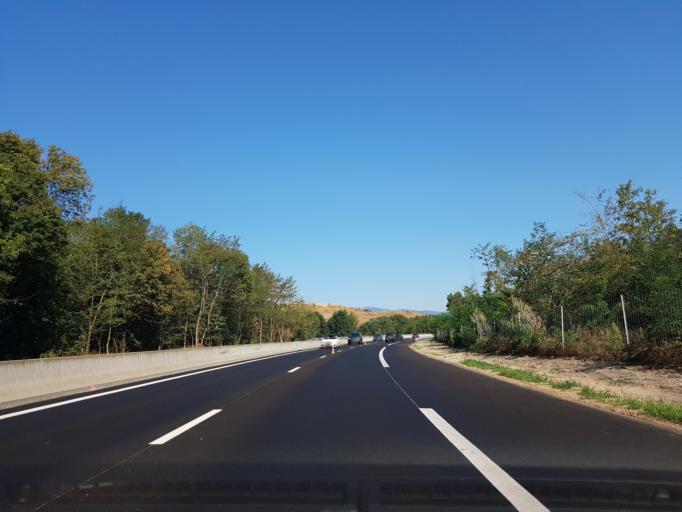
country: FR
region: Alsace
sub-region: Departement du Haut-Rhin
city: Pulversheim
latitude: 47.8318
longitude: 7.2774
